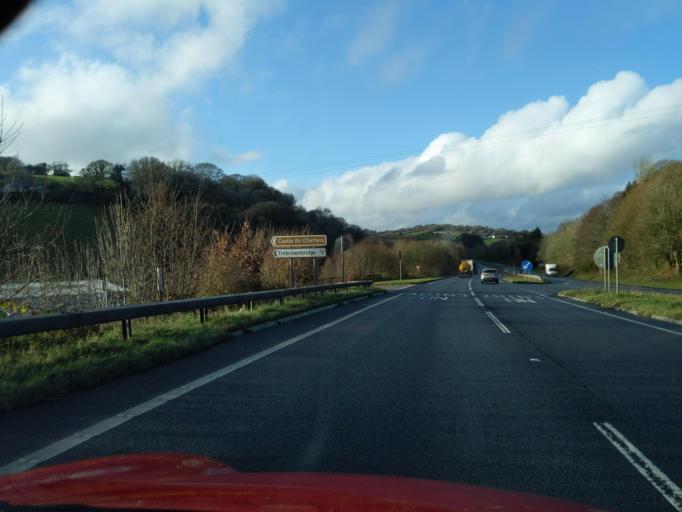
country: GB
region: England
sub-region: Cornwall
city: Liskeard
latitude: 50.4165
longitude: -4.3950
